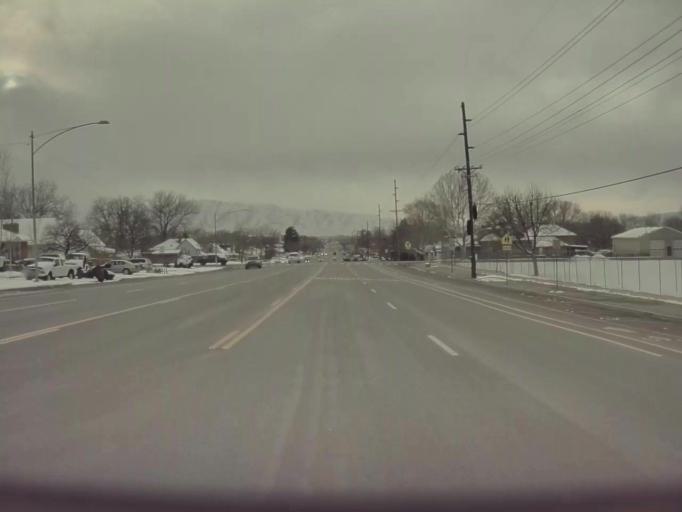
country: US
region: Utah
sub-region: Utah County
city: Spanish Fork
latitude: 40.1098
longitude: -111.6426
